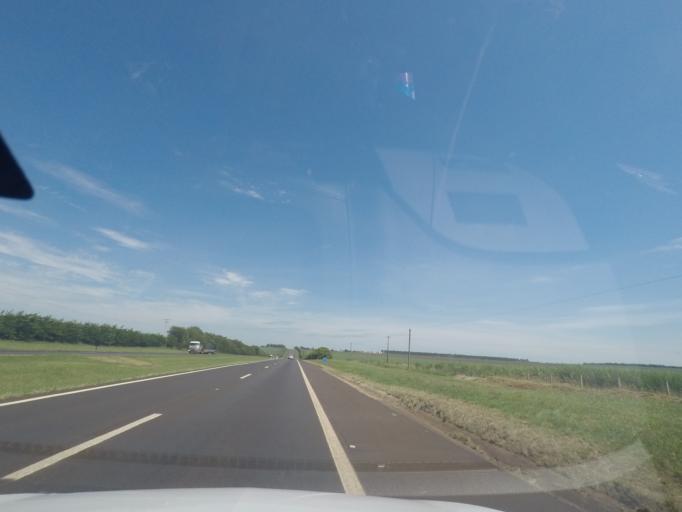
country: BR
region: Sao Paulo
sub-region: Araraquara
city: Araraquara
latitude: -21.8543
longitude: -48.1282
